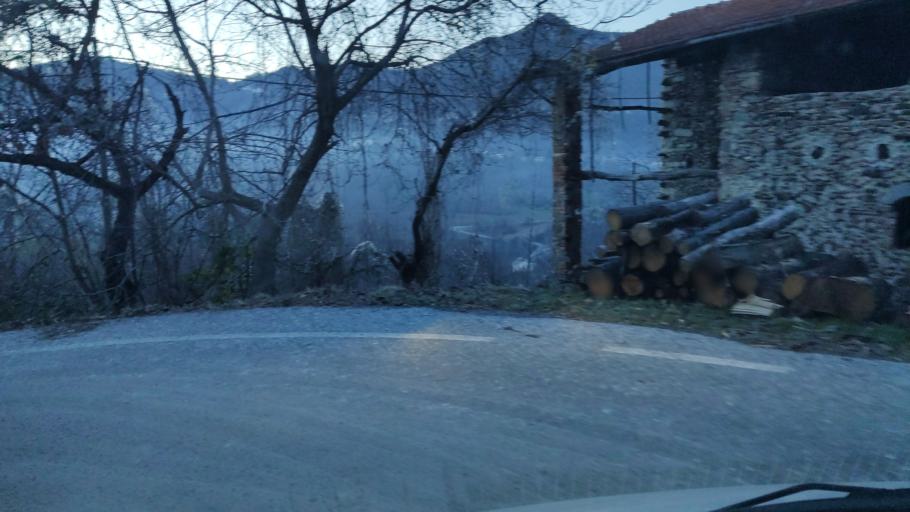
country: IT
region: Piedmont
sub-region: Provincia di Cuneo
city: Lisio
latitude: 44.2909
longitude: 7.9831
